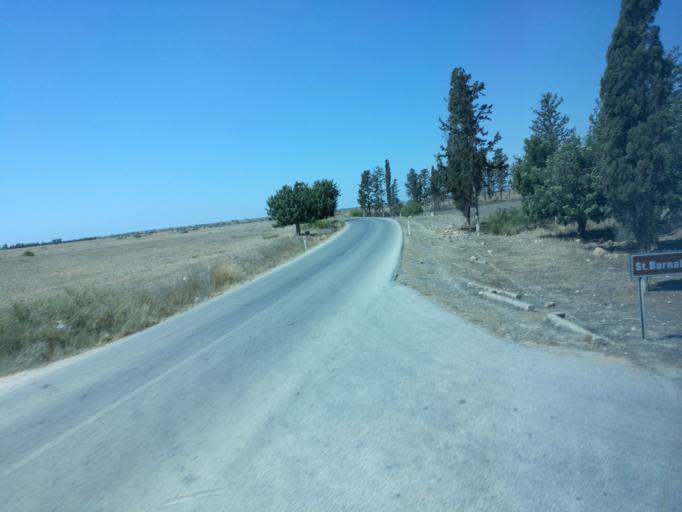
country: CY
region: Ammochostos
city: Acheritou
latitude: 35.1742
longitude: 33.8814
